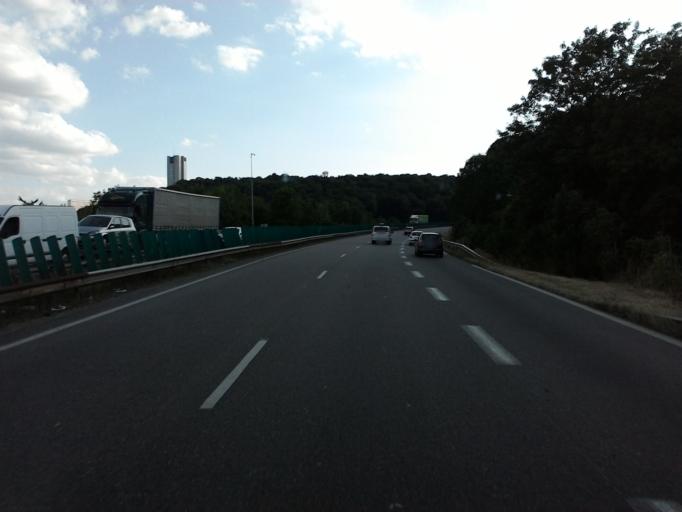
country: FR
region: Lorraine
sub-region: Departement de Meurthe-et-Moselle
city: Maxeville
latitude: 48.7161
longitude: 6.1624
